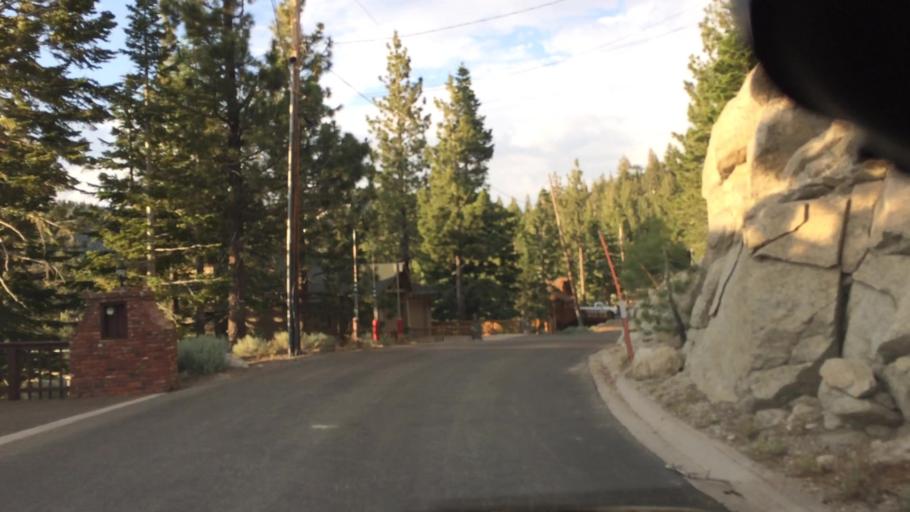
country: US
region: Nevada
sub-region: Douglas County
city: Kingsbury
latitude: 38.9699
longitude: -119.8923
